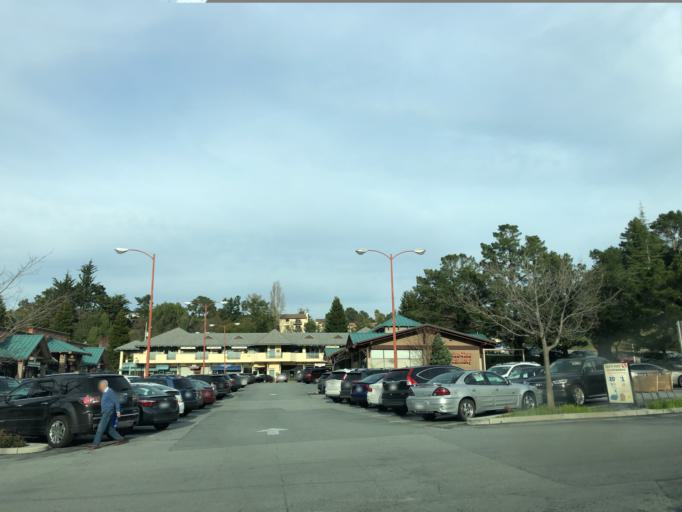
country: US
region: California
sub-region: San Mateo County
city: Highlands-Baywood Park
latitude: 37.5205
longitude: -122.3375
